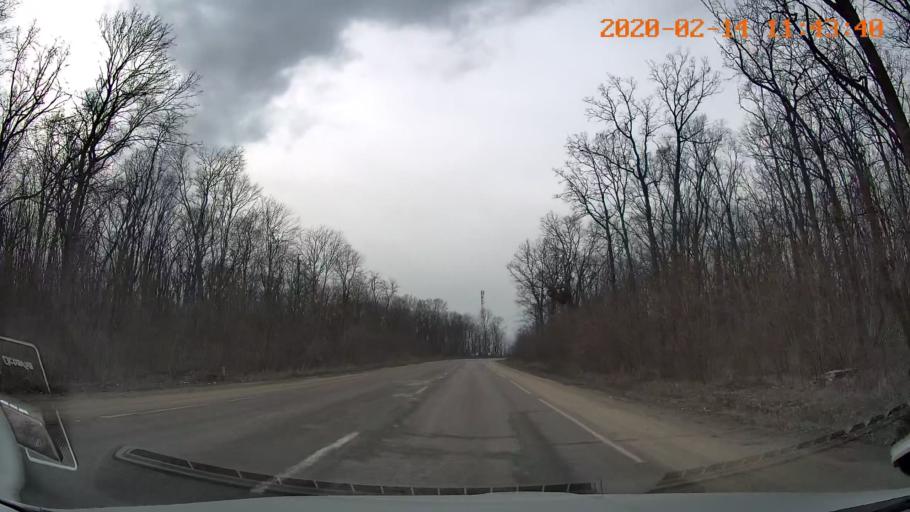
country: MD
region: Briceni
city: Briceni
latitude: 48.3320
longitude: 27.0488
